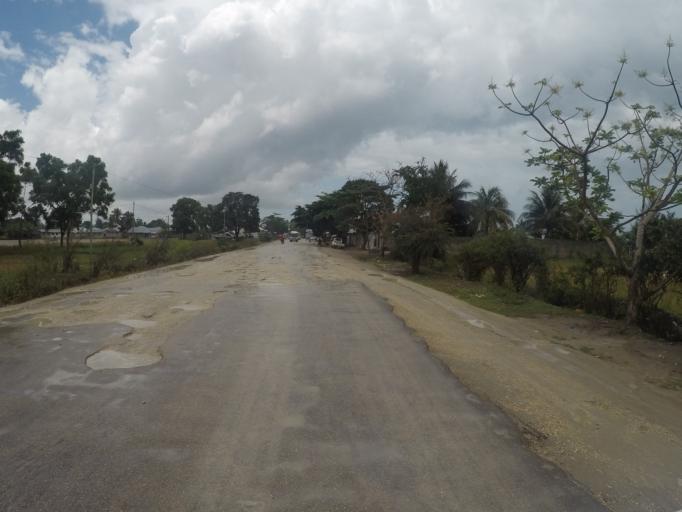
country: TZ
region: Zanzibar Central/South
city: Koani
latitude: -6.0785
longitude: 39.2222
